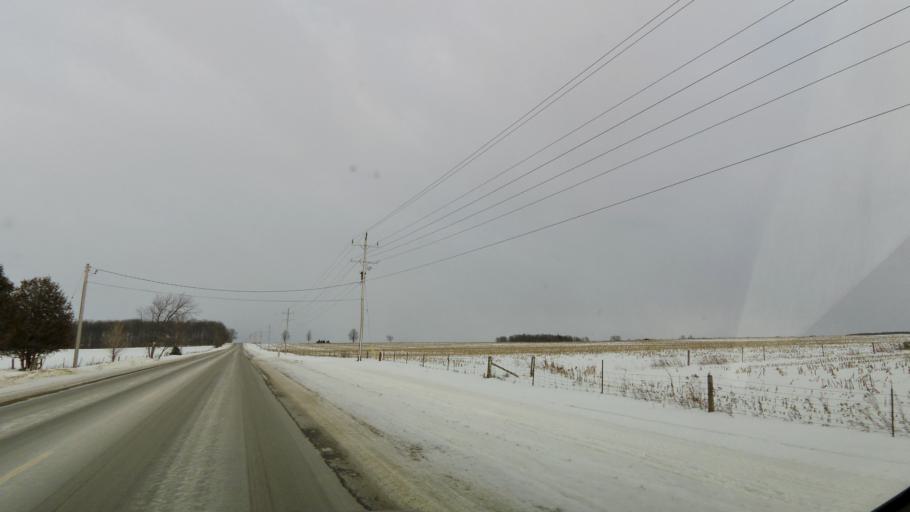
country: CA
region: Ontario
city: Omemee
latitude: 44.4885
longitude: -78.8664
